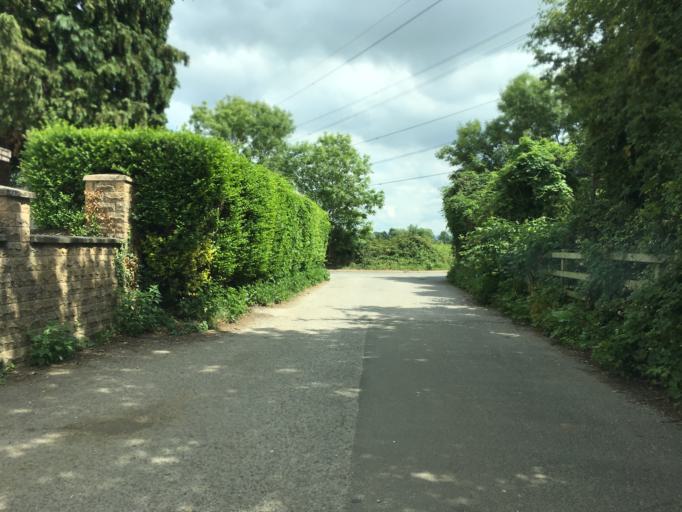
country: GB
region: England
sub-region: Gloucestershire
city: Gloucester
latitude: 51.8823
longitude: -2.2487
